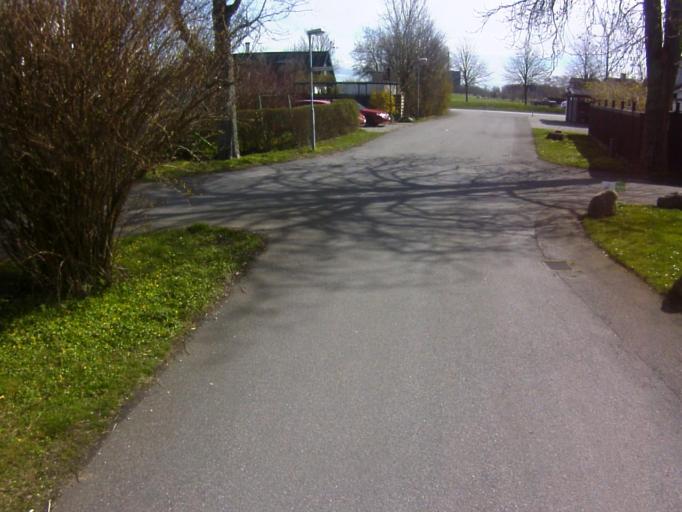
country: SE
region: Skane
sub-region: Kavlinge Kommun
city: Hofterup
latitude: 55.7575
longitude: 12.9092
